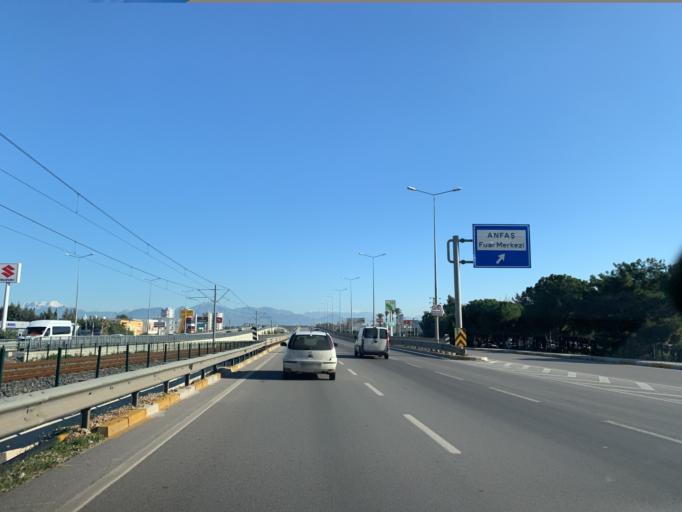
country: TR
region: Antalya
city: Aksu
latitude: 36.9340
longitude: 30.8119
